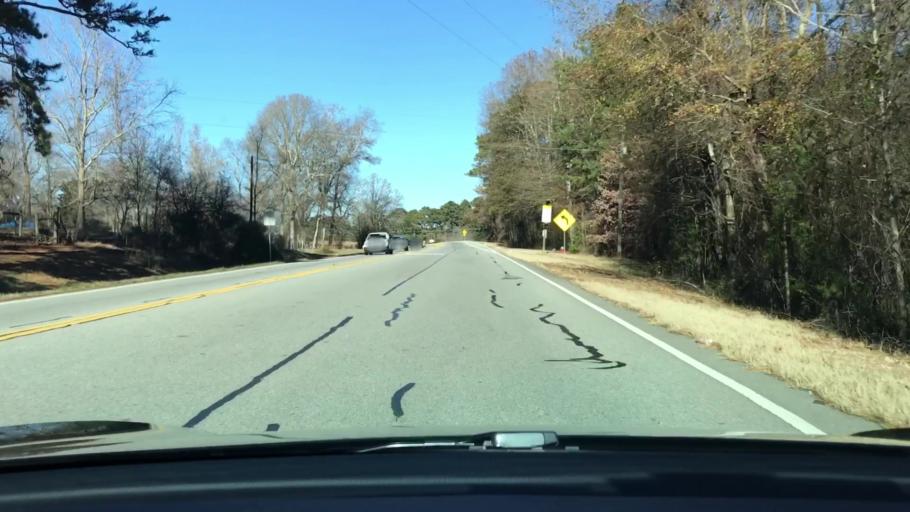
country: US
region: Georgia
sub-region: Barrow County
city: Russell
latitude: 33.9169
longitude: -83.7168
